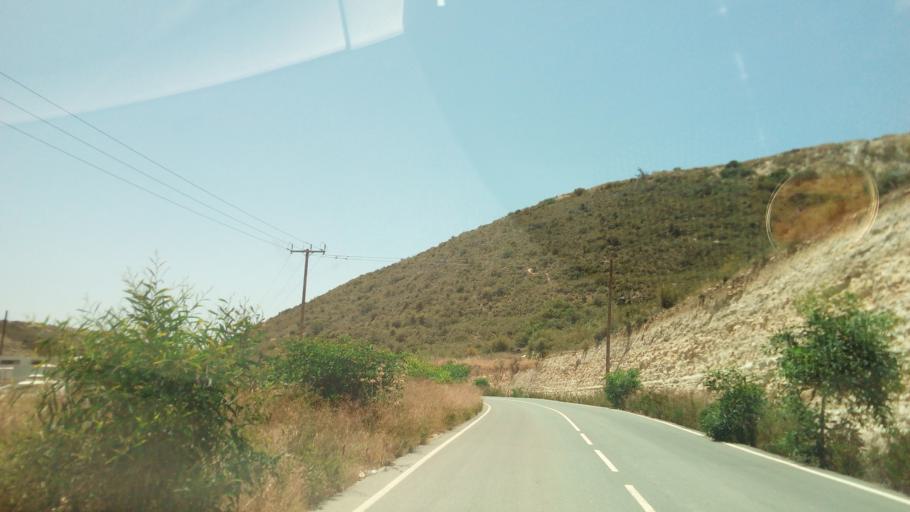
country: CY
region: Limassol
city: Ypsonas
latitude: 34.7415
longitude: 32.9446
